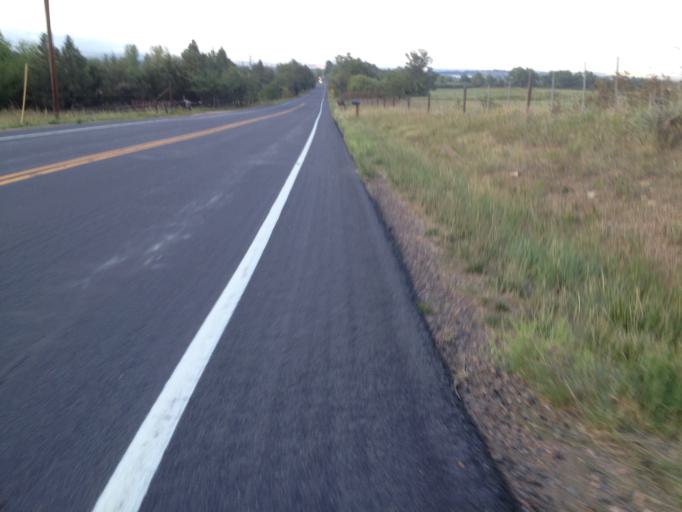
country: US
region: Colorado
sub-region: Boulder County
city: Superior
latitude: 39.9655
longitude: -105.2129
